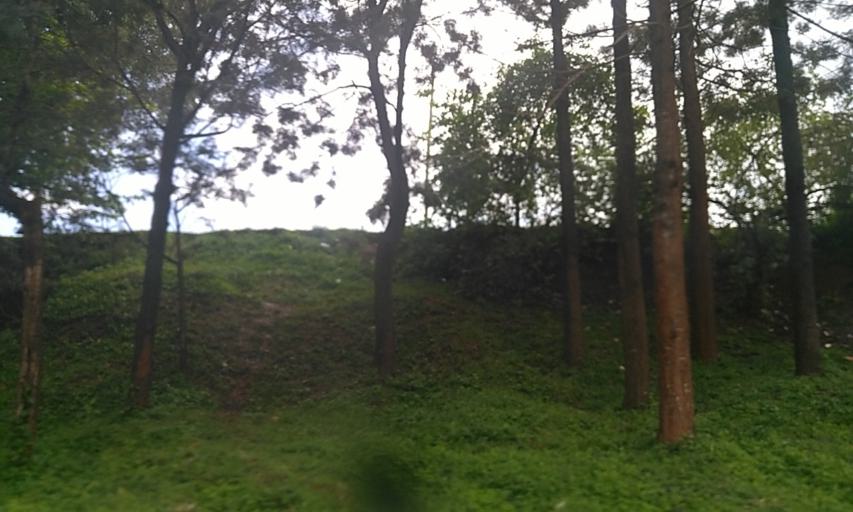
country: UG
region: Central Region
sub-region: Kampala District
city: Kampala
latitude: 0.3256
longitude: 32.5924
